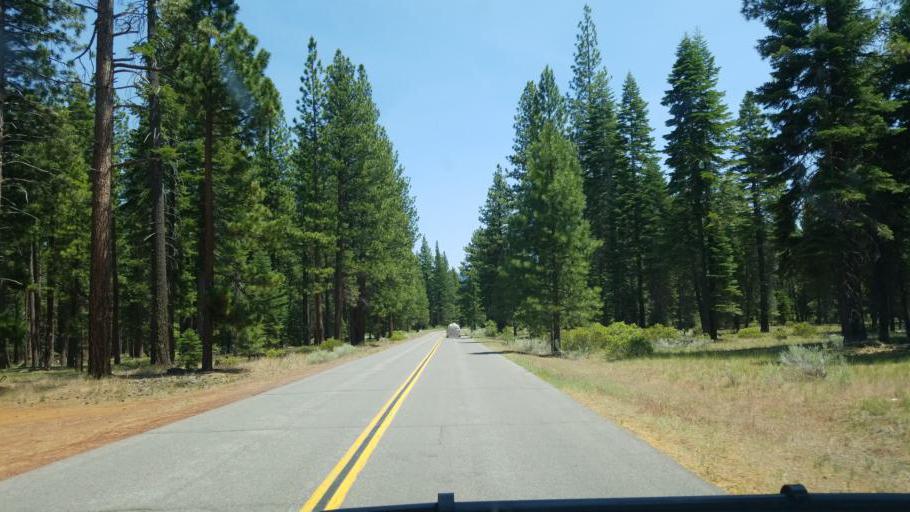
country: US
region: California
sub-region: Lassen County
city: Susanville
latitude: 40.5470
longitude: -120.8049
